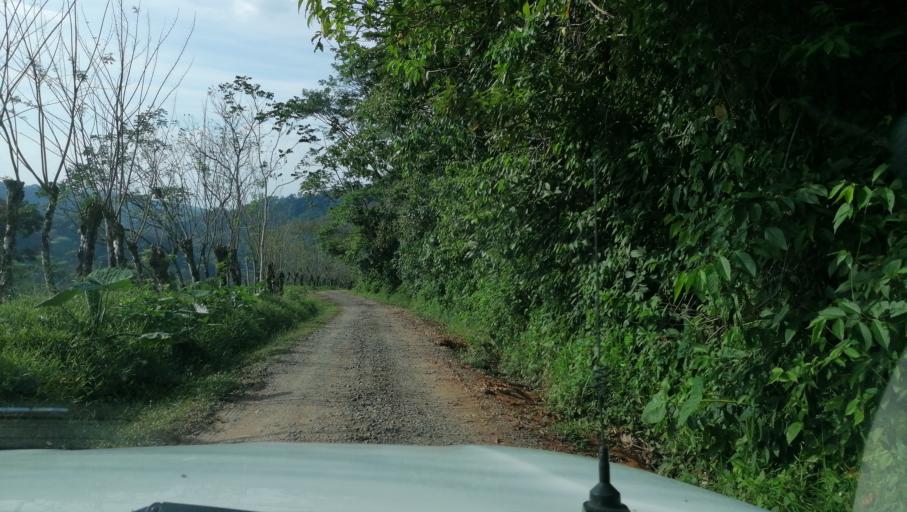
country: MX
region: Chiapas
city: Ostuacan
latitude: 17.4676
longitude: -93.2336
